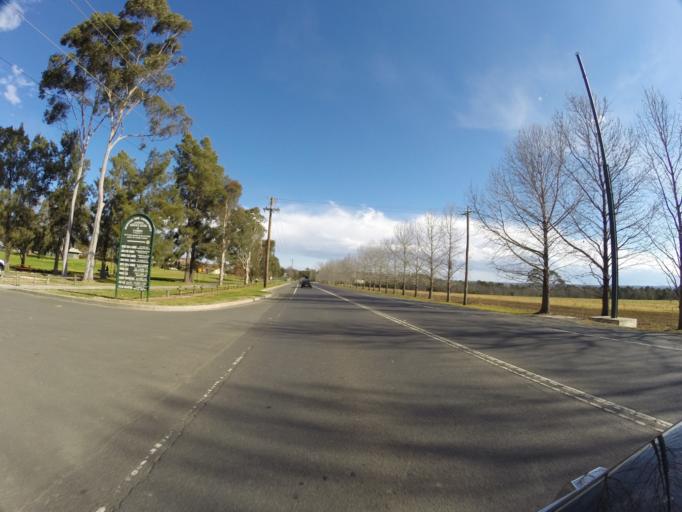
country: AU
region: New South Wales
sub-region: Camden
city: Elderslie
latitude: -34.0527
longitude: 150.7092
